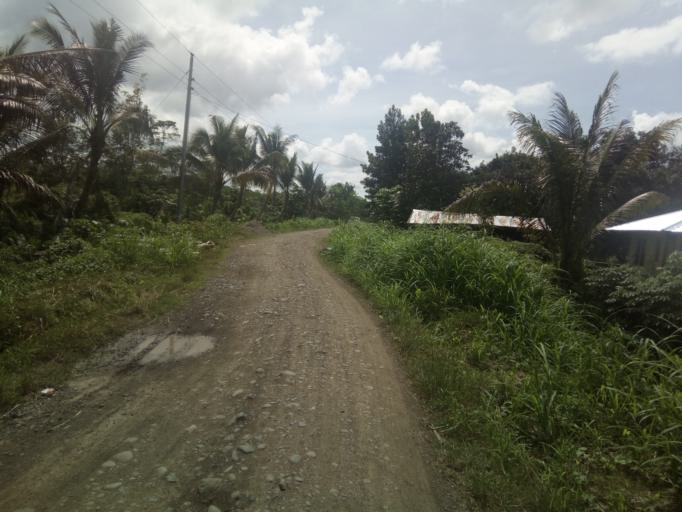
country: PH
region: Caraga
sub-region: Province of Agusan del Sur
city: Trento
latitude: 8.0470
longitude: 126.0122
